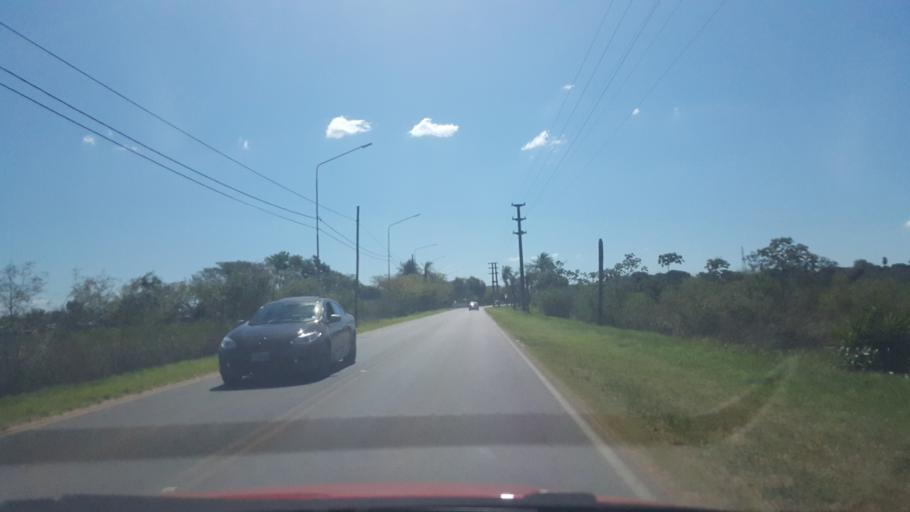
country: AR
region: Corrientes
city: Ituzaingo
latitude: -27.5940
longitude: -56.6816
